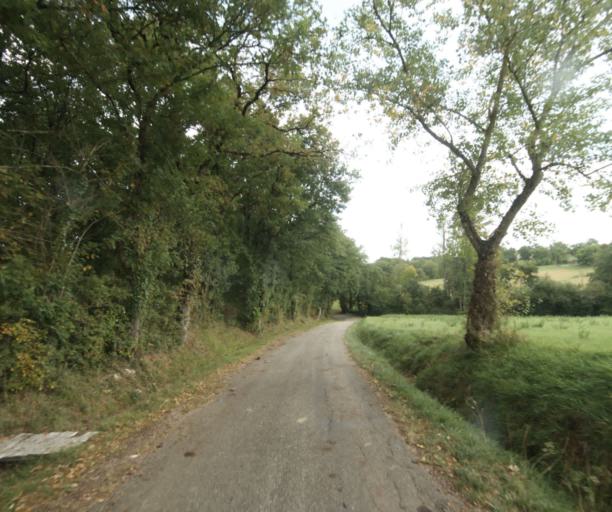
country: FR
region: Midi-Pyrenees
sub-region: Departement du Gers
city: Gondrin
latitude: 43.8650
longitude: 0.2595
